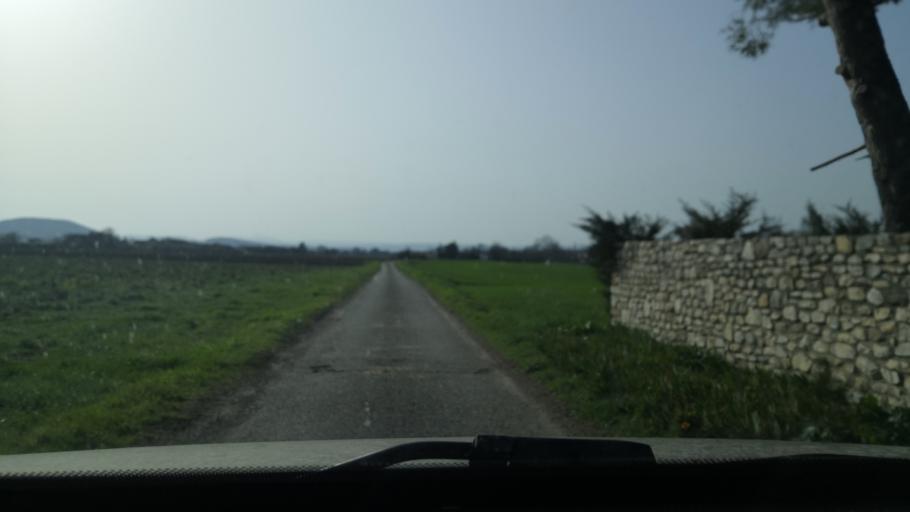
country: FR
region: Rhone-Alpes
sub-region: Departement de la Drome
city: Montboucher-sur-Jabron
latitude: 44.5582
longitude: 4.8581
